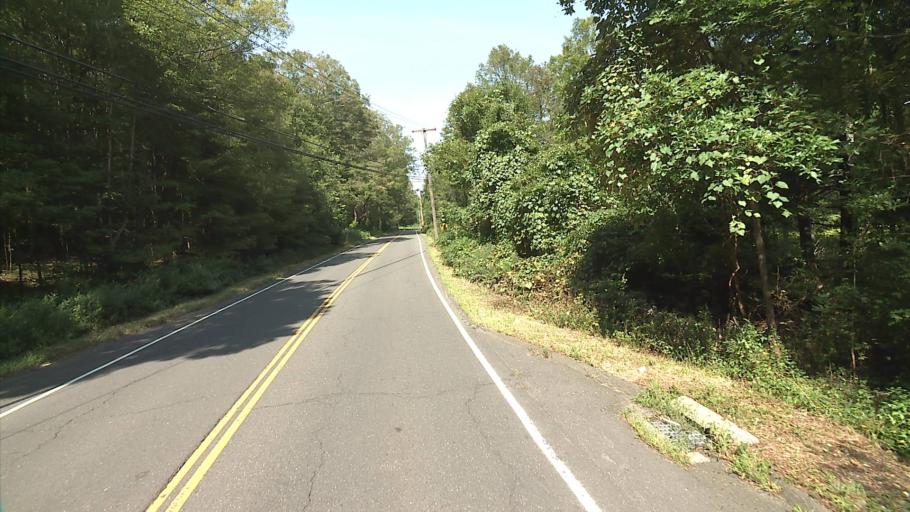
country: US
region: Connecticut
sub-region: Fairfield County
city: Georgetown
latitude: 41.2514
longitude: -73.3232
